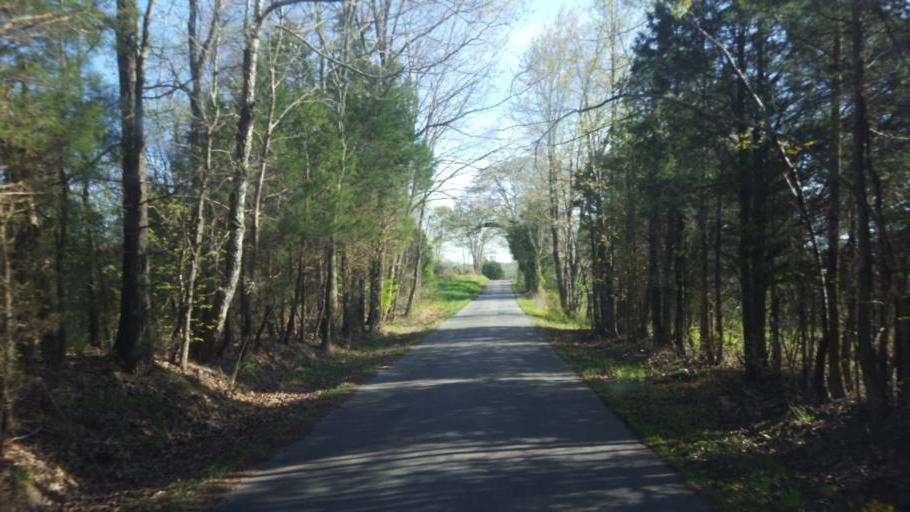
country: US
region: Kentucky
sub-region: Barren County
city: Cave City
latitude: 37.1766
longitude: -85.9973
